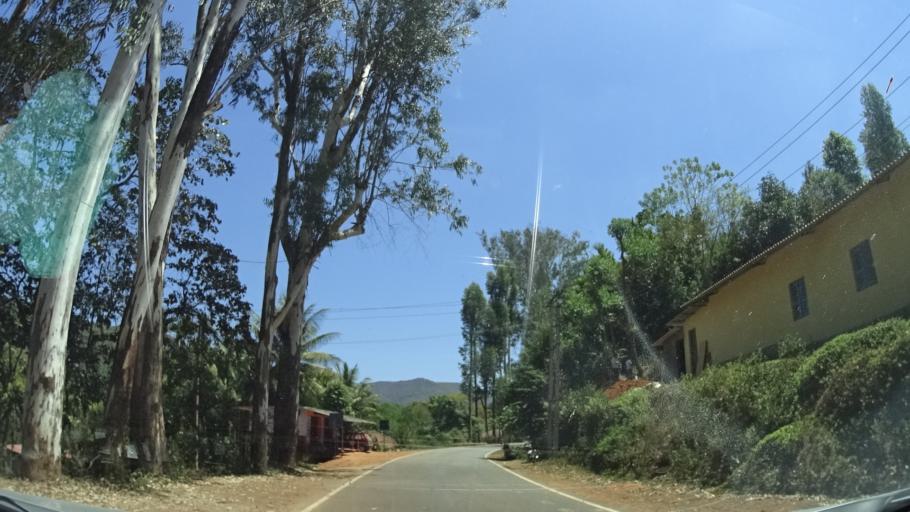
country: IN
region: Karnataka
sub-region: Chikmagalur
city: Sringeri
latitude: 13.2053
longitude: 75.2821
